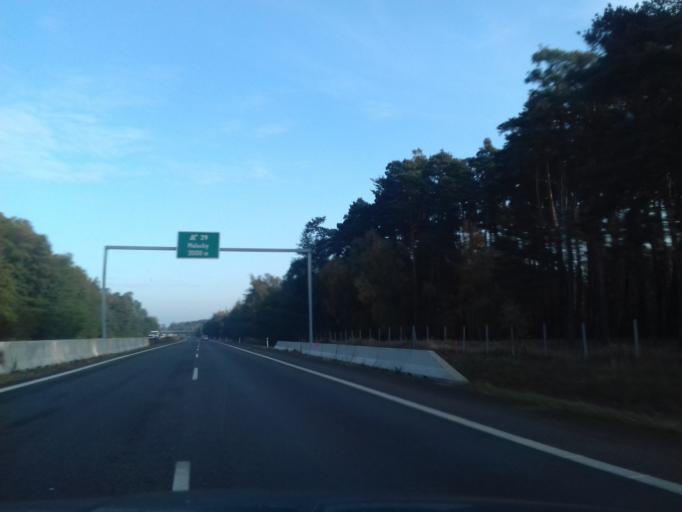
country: SK
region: Bratislavsky
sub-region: Okres Malacky
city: Malacky
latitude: 48.4065
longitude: 17.0335
